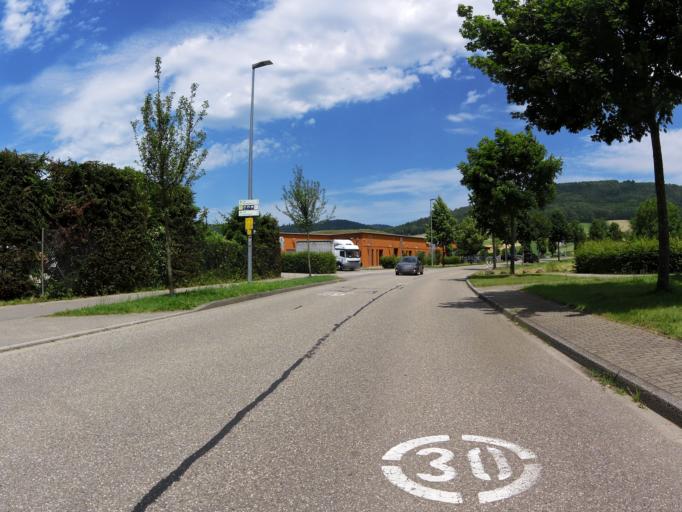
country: DE
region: Baden-Wuerttemberg
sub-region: Freiburg Region
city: Seelbach
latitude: 48.3187
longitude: 7.9357
